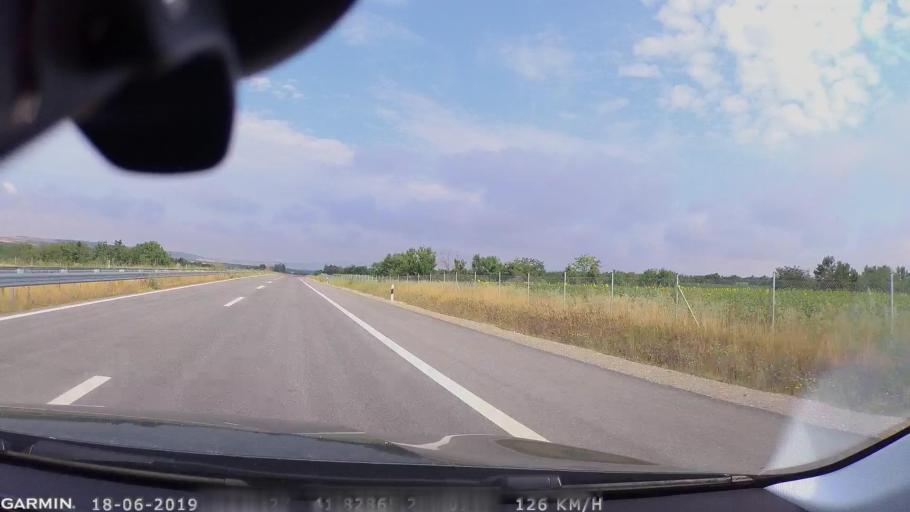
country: MK
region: Sveti Nikole
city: Sveti Nikole
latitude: 41.8287
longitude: 22.0017
